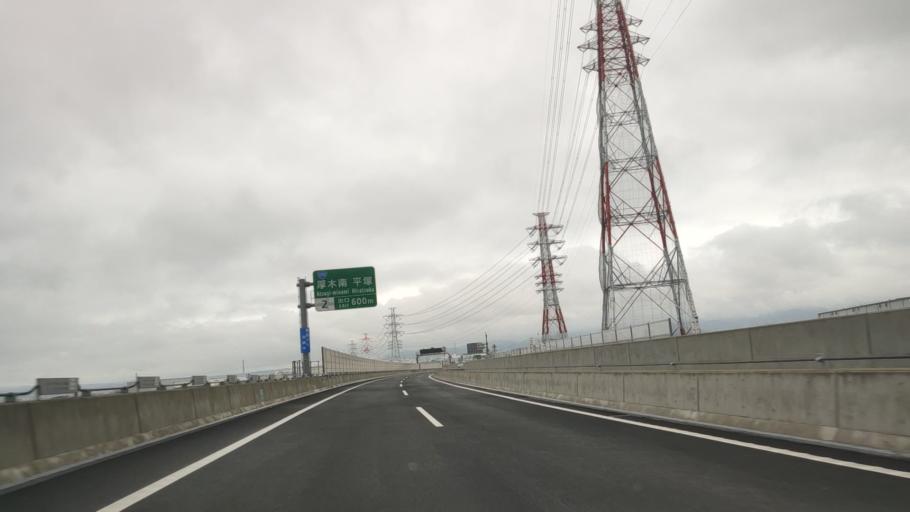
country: JP
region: Kanagawa
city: Atsugi
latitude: 35.4069
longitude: 139.3670
